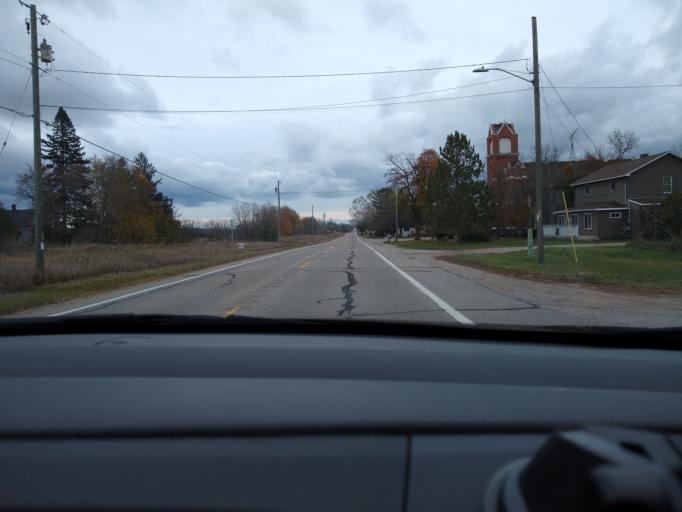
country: US
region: Michigan
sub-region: Delta County
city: Escanaba
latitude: 45.7609
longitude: -87.2980
